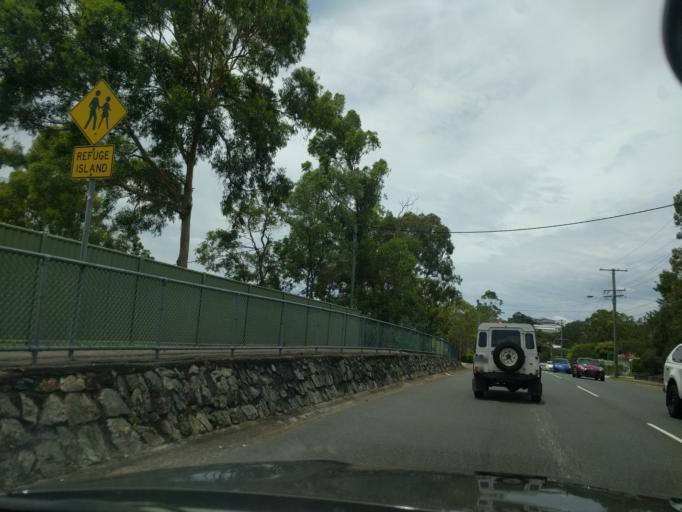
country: AU
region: Queensland
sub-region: Brisbane
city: Stafford
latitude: -27.4108
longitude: 153.0075
